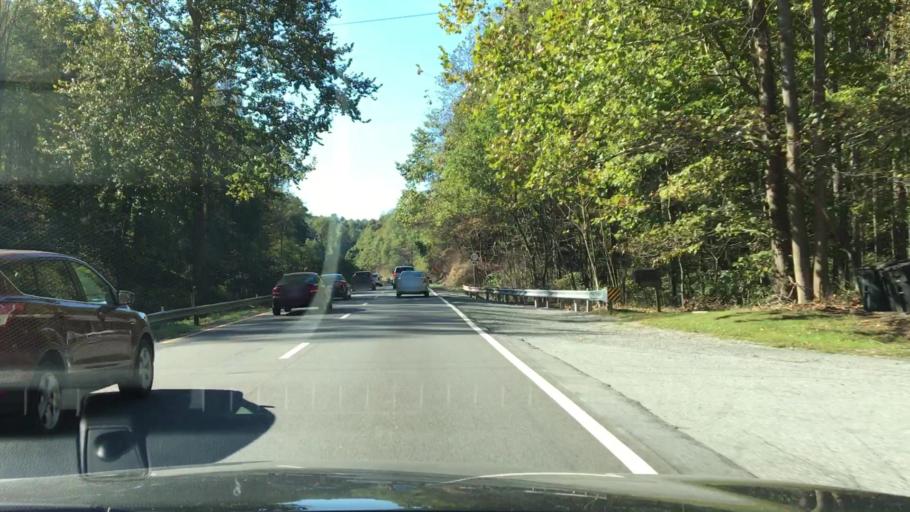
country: US
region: Virginia
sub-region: Roanoke County
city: Narrows
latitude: 37.1561
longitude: -79.9542
